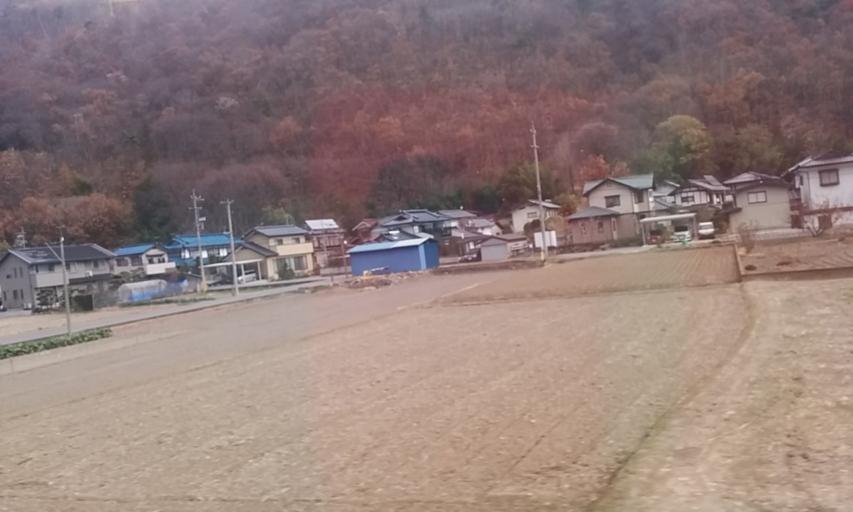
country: JP
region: Nagano
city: Nagano-shi
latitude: 36.5035
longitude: 138.1467
